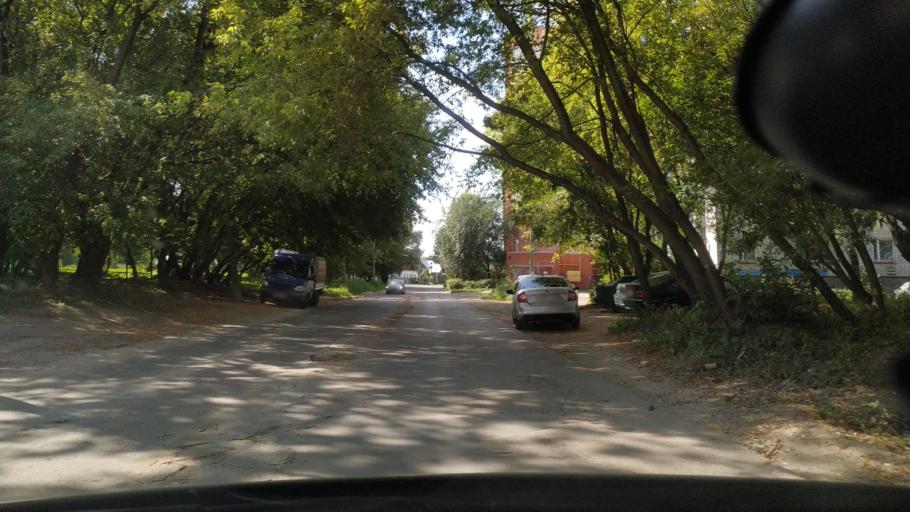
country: RU
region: Rjazan
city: Ryazan'
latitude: 54.6182
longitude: 39.7084
